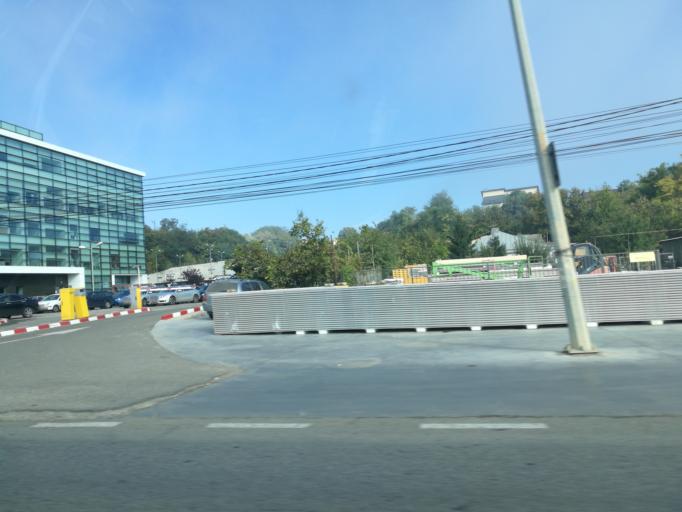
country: RO
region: Iasi
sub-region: Comuna Miroslava
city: Miroslava
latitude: 47.1726
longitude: 27.5237
